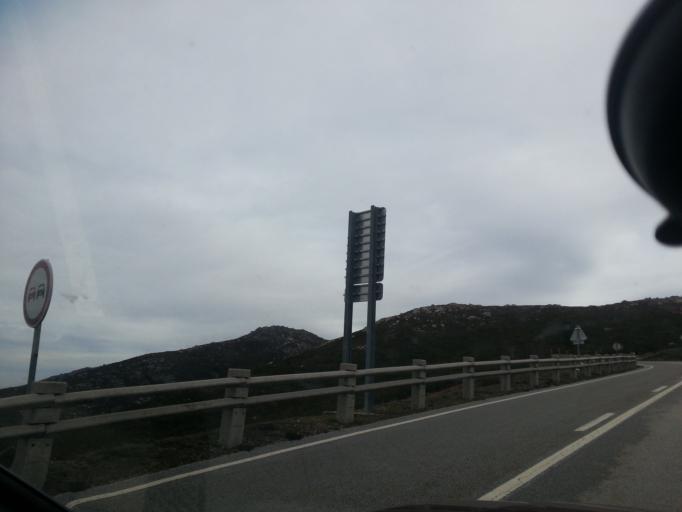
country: PT
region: Guarda
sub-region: Seia
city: Seia
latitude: 40.3445
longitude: -7.7003
